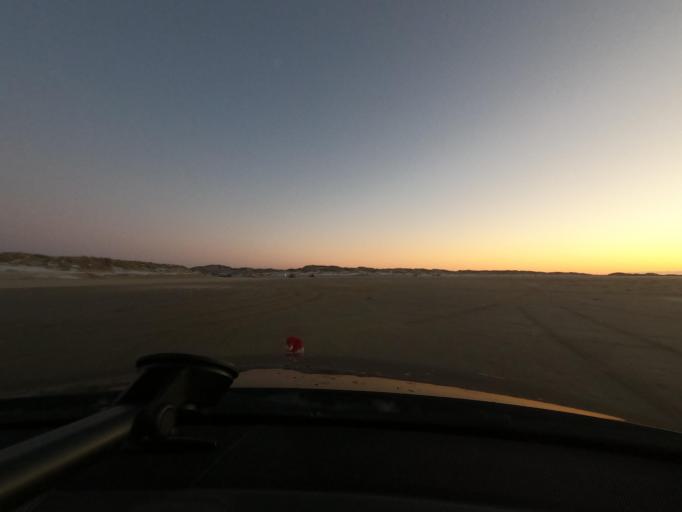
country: DE
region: Schleswig-Holstein
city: List
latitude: 55.1466
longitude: 8.4864
